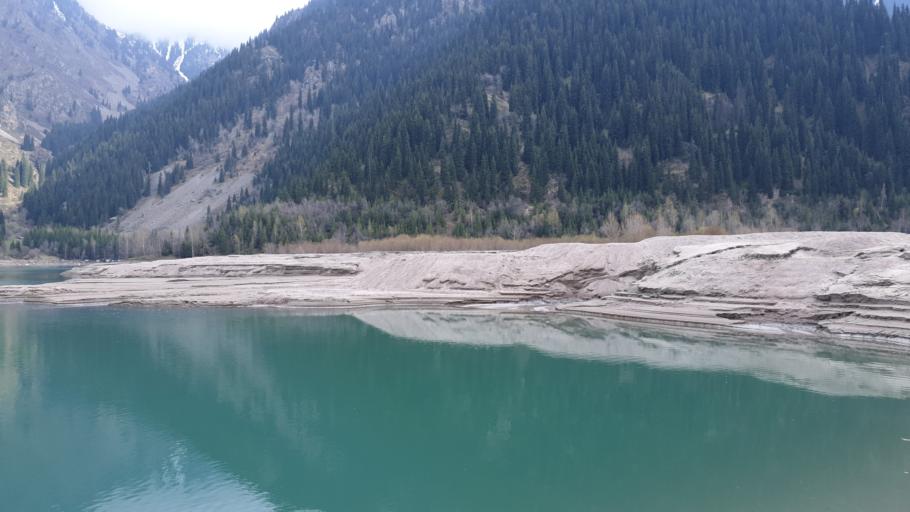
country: KZ
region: Almaty Oblysy
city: Esik
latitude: 43.2540
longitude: 77.4817
